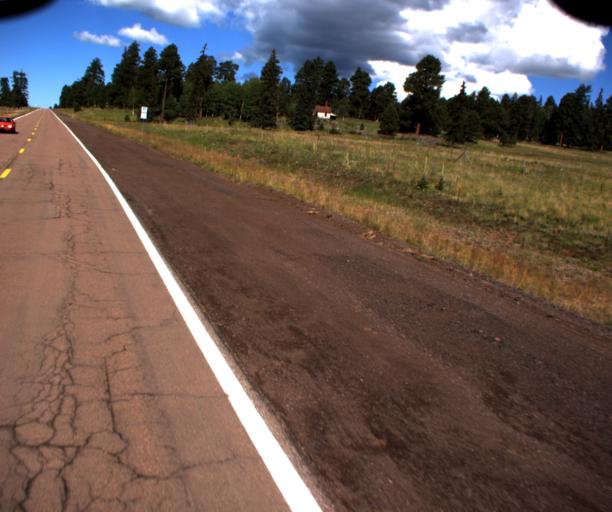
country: US
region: Arizona
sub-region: Apache County
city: Eagar
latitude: 34.0545
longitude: -109.5503
